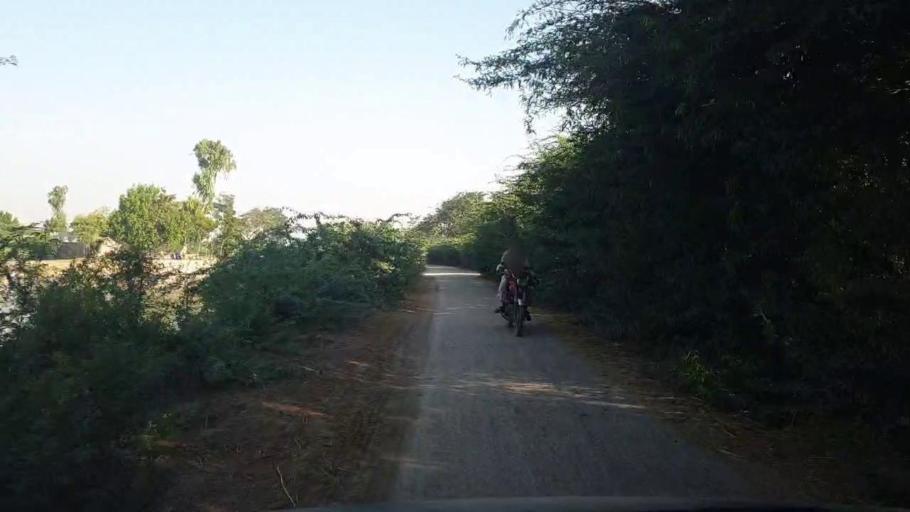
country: PK
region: Sindh
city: Badin
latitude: 24.6880
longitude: 68.8163
